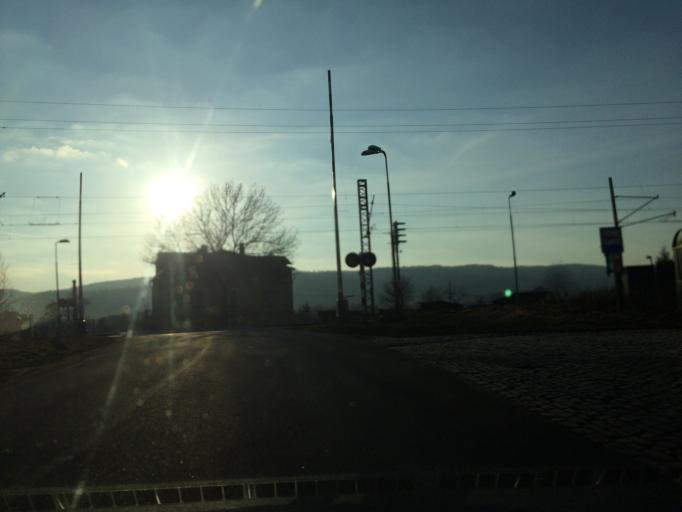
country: PL
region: Lower Silesian Voivodeship
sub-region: Powiat klodzki
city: Miedzylesie
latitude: 50.2118
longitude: 16.6564
